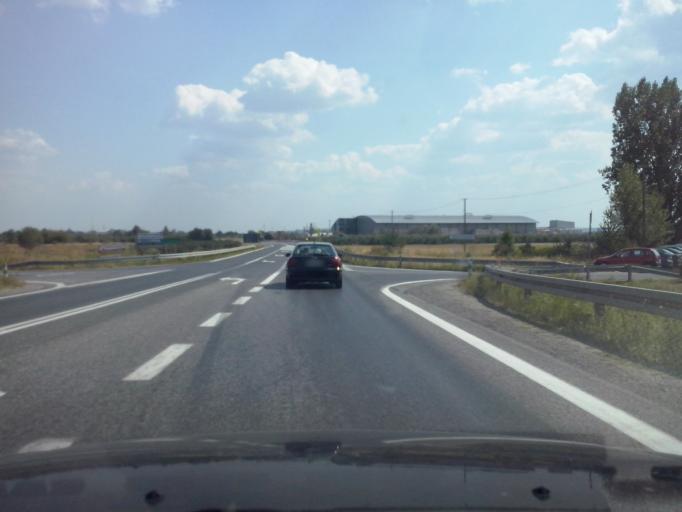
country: PL
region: Swietokrzyskie
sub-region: Powiat sandomierski
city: Loniow
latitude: 50.5470
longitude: 21.5490
